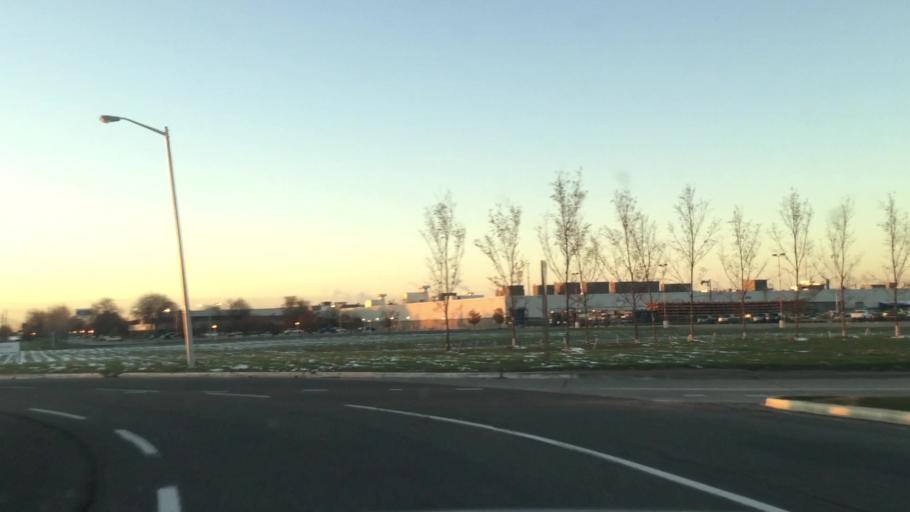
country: US
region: Michigan
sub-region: Macomb County
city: Sterling Heights
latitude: 42.6016
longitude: -83.0315
